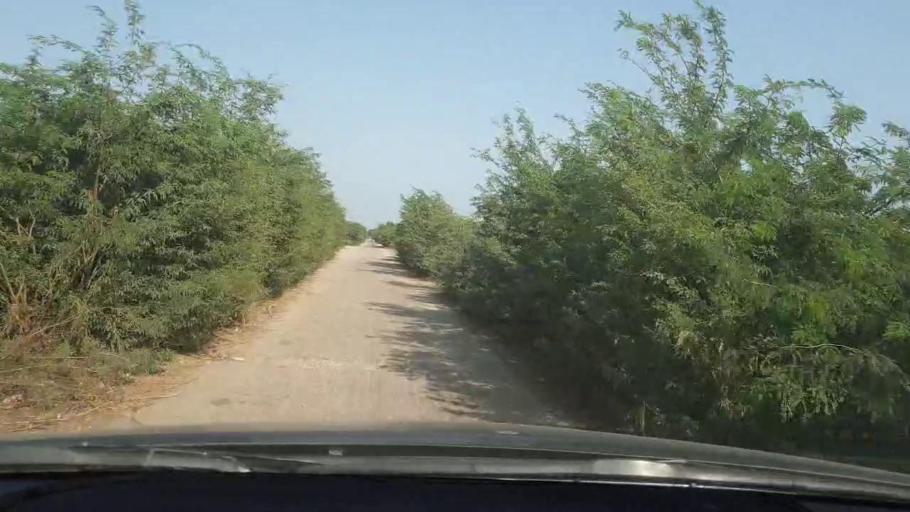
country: PK
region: Sindh
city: Naukot
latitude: 24.7666
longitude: 69.2448
